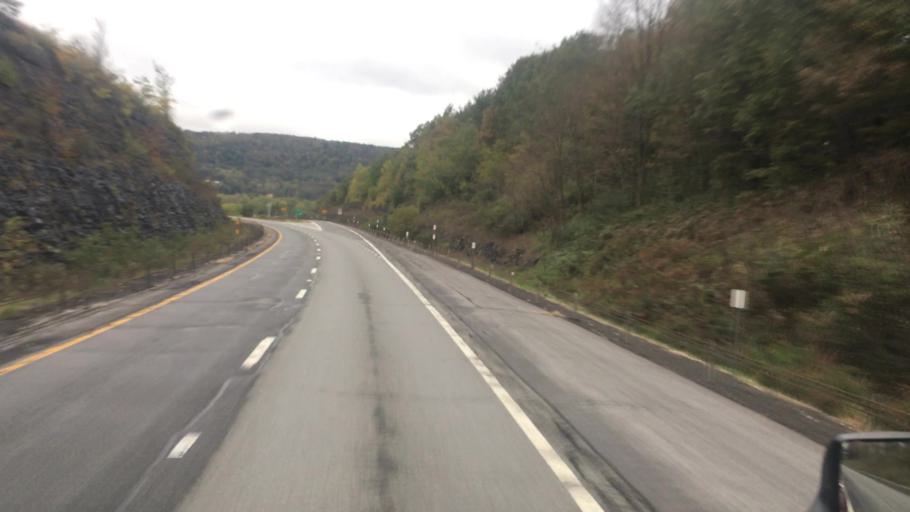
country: US
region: New York
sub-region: Chenango County
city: Bainbridge
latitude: 42.2942
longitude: -75.4654
